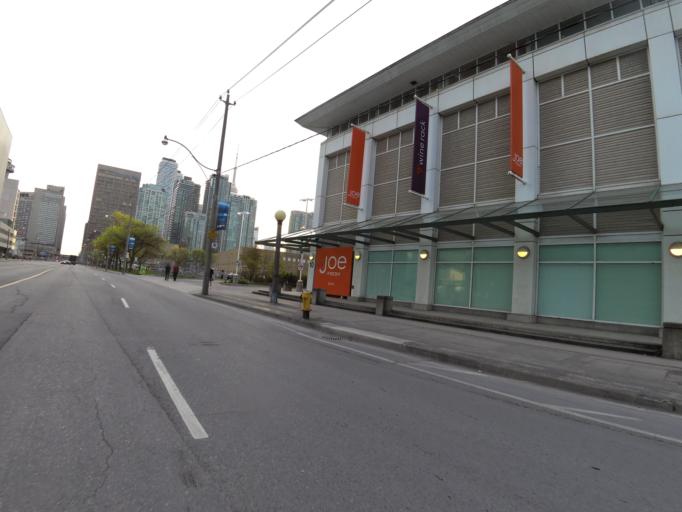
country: CA
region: Ontario
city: Toronto
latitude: 43.6438
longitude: -79.3696
